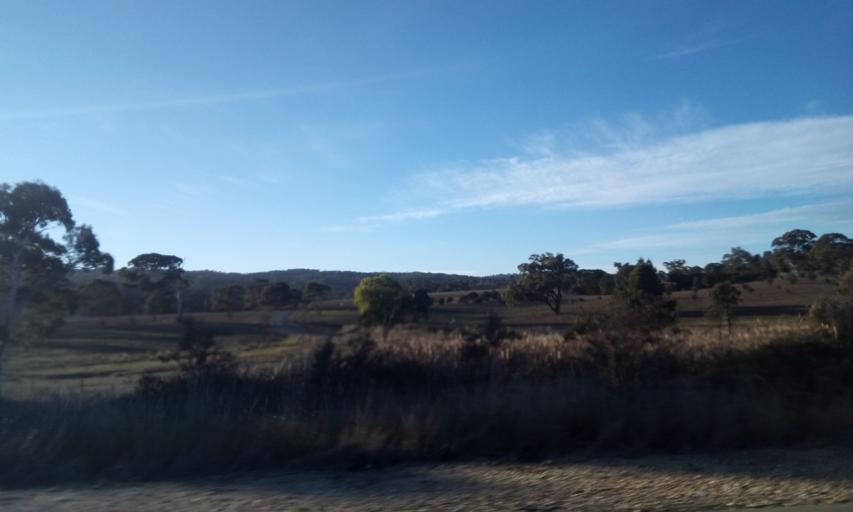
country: AU
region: New South Wales
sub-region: Yass Valley
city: Gundaroo
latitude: -35.1214
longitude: 149.3460
